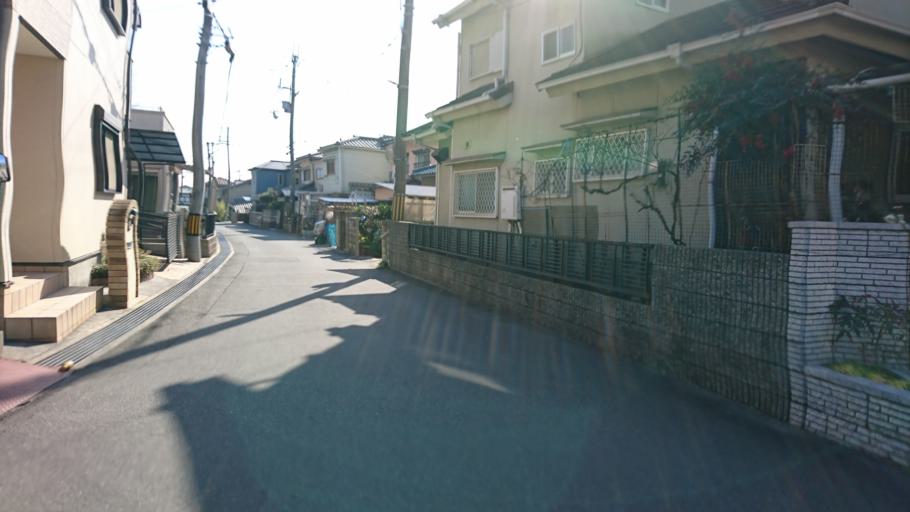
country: JP
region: Hyogo
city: Kakogawacho-honmachi
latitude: 34.7814
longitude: 134.7882
